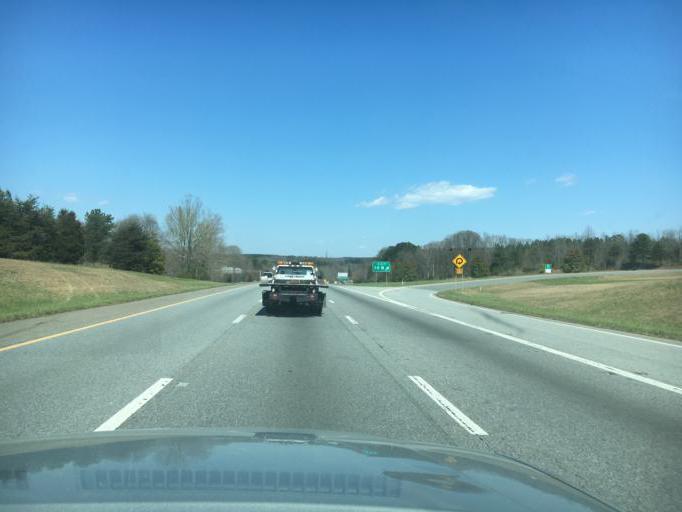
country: US
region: North Carolina
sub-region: Gaston County
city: Bessemer City
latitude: 35.2502
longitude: -81.2980
